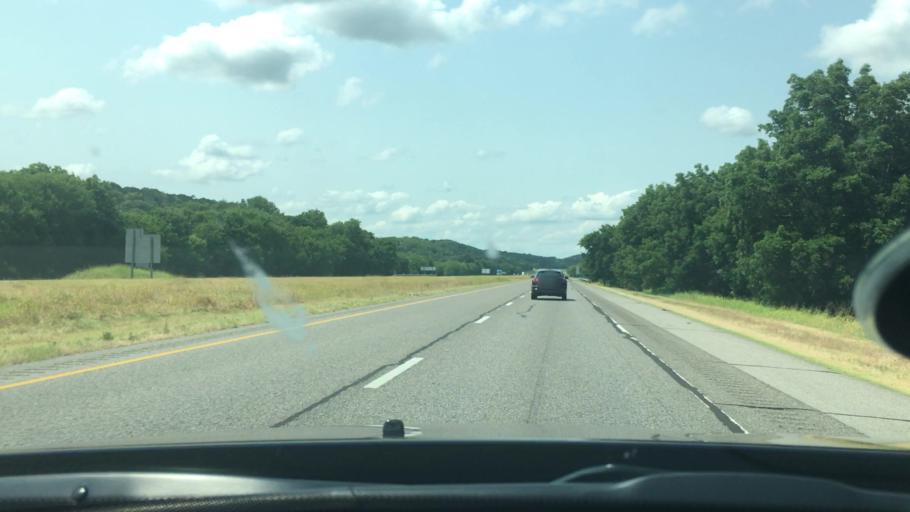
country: US
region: Oklahoma
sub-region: Murray County
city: Davis
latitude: 34.4556
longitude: -97.1398
